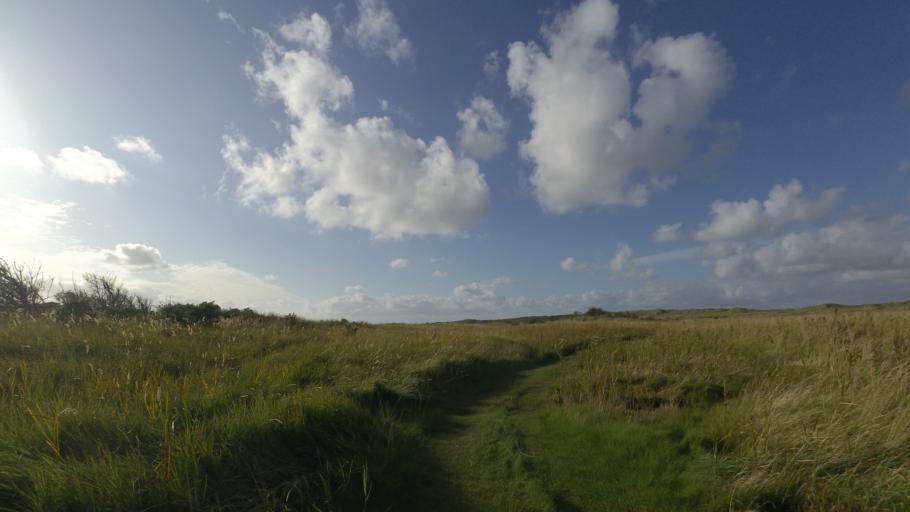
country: NL
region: Friesland
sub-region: Gemeente Dongeradeel
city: Ternaard
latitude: 53.4617
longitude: 5.9175
